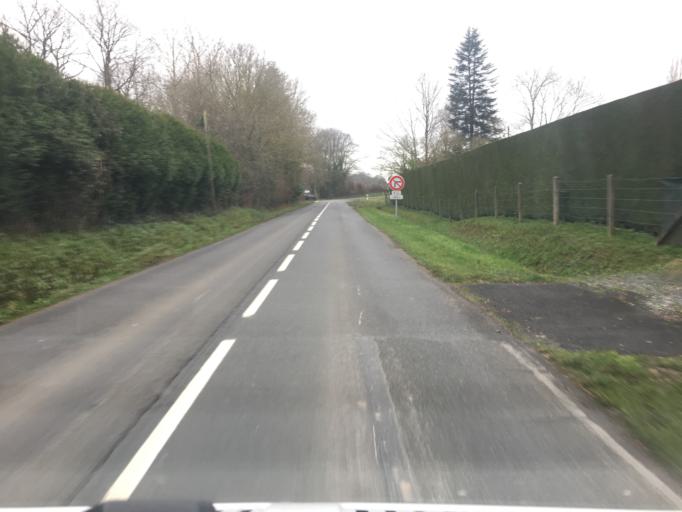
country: FR
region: Lower Normandy
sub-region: Departement du Calvados
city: Dozule
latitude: 49.2696
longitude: -0.0394
